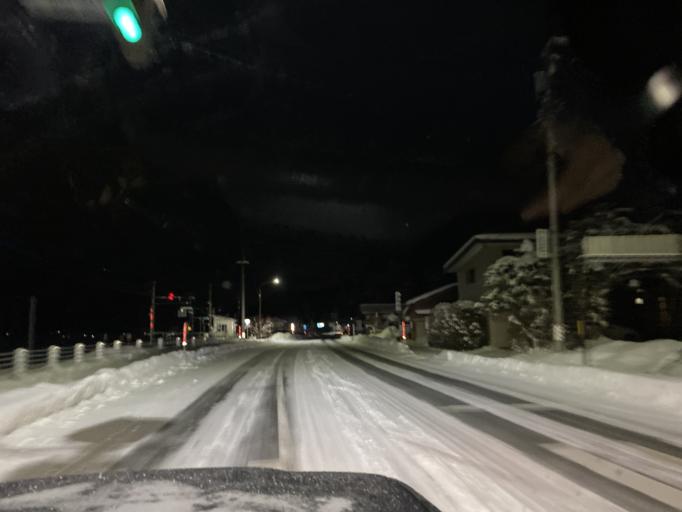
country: JP
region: Nagano
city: Omachi
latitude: 36.5534
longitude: 137.8427
